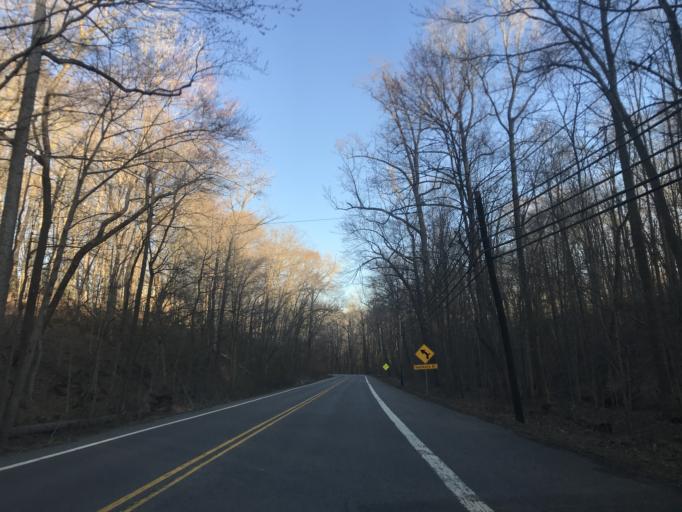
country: US
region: Maryland
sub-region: Anne Arundel County
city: Crofton
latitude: 38.9909
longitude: -76.6536
